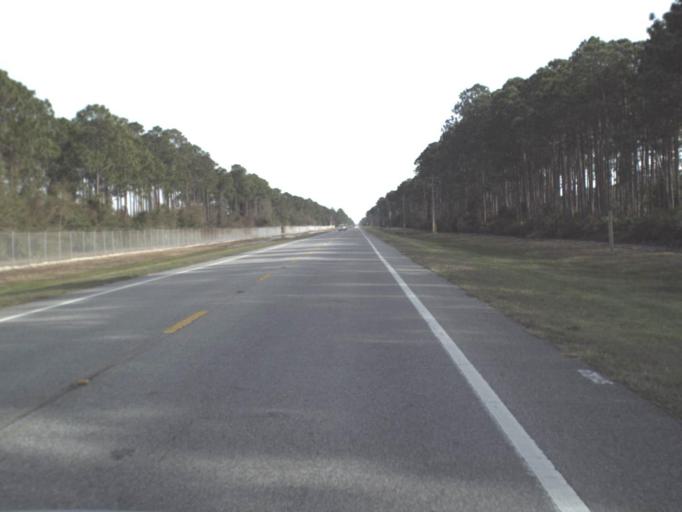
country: US
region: Florida
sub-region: Bay County
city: Tyndall Air Force Base
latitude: 30.0567
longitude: -85.5730
